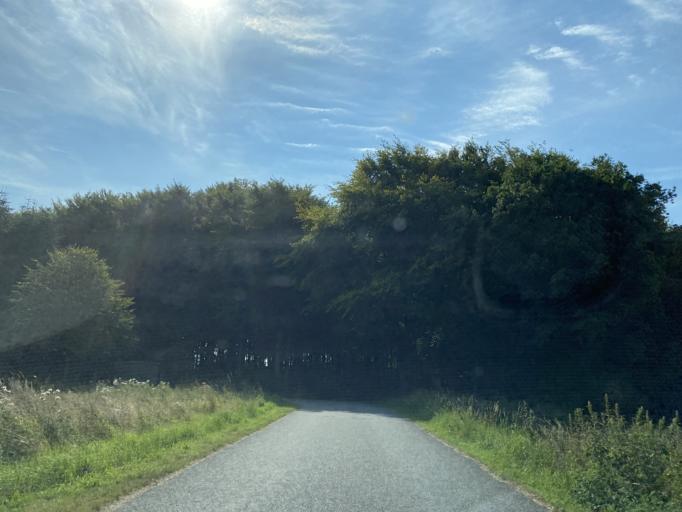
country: DK
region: Central Jutland
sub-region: Viborg Kommune
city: Bjerringbro
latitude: 56.3423
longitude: 9.7253
